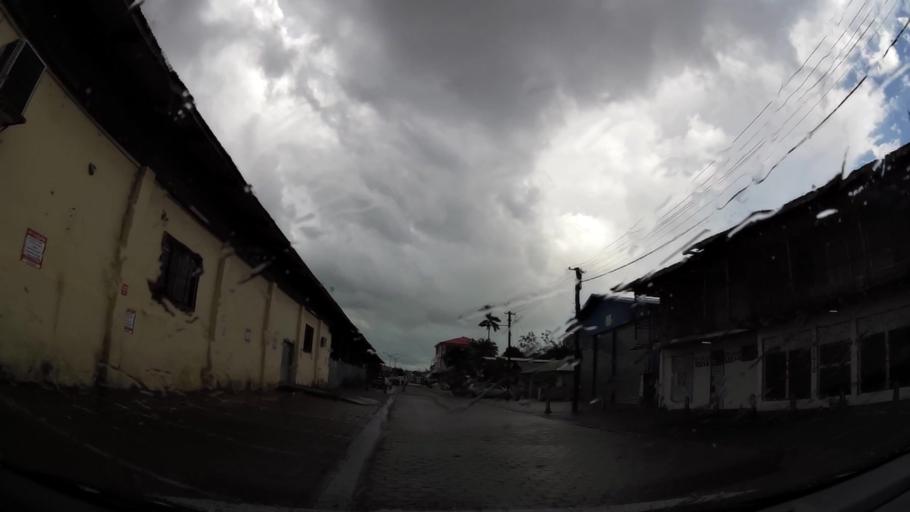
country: SR
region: Paramaribo
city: Paramaribo
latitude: 5.8219
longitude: -55.1660
